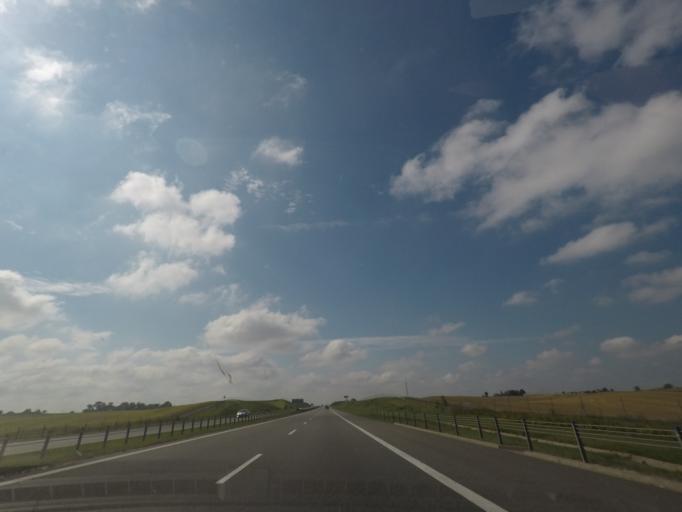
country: PL
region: Kujawsko-Pomorskie
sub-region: Powiat chelminski
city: Lisewo
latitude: 53.3280
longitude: 18.7080
